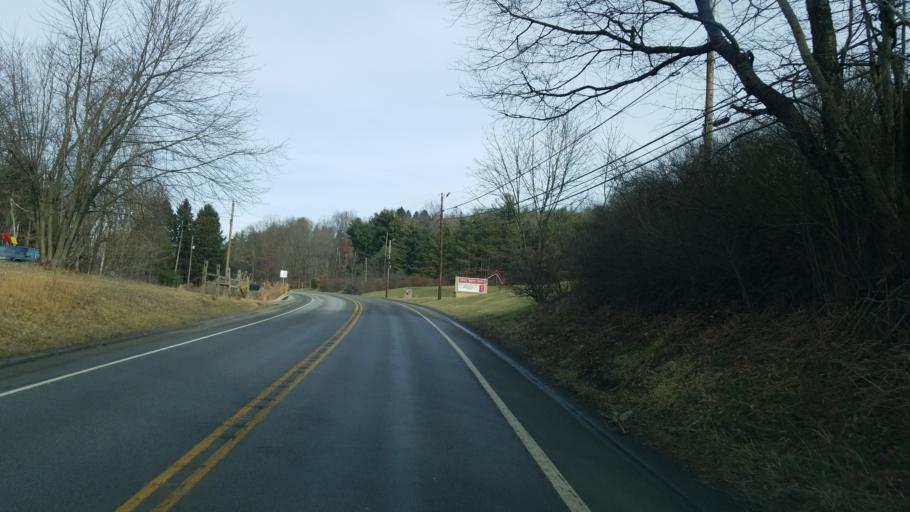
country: US
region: Pennsylvania
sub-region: Indiana County
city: Clymer
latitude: 40.6984
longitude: -78.9884
